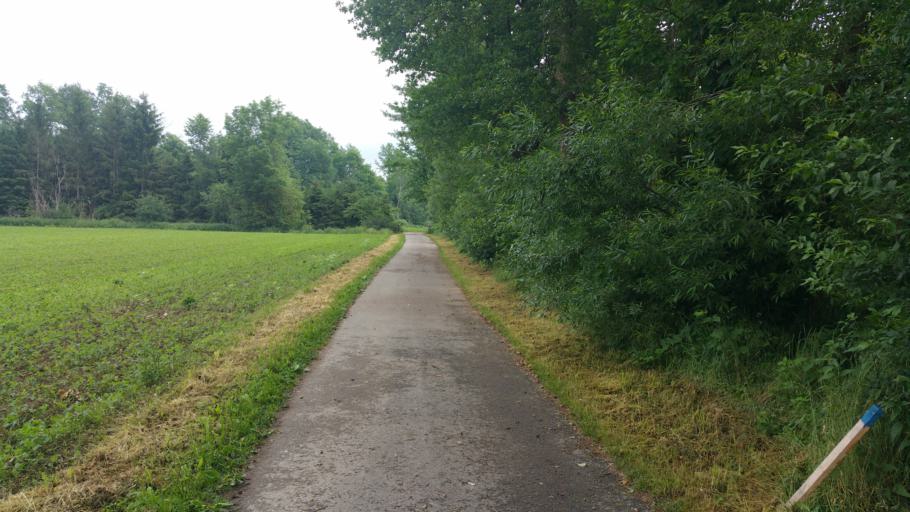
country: AT
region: Styria
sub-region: Politischer Bezirk Leibnitz
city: Gleinstatten
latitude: 46.7553
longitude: 15.3748
